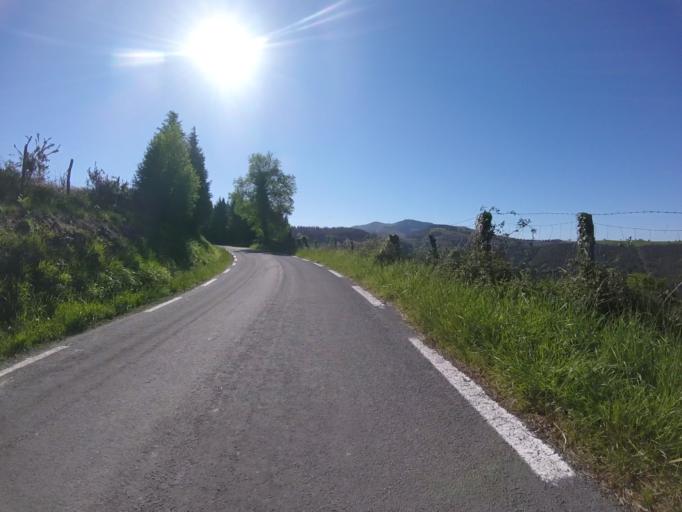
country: ES
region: Basque Country
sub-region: Provincia de Guipuzcoa
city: Aizarnazabal
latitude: 43.2143
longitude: -2.2080
